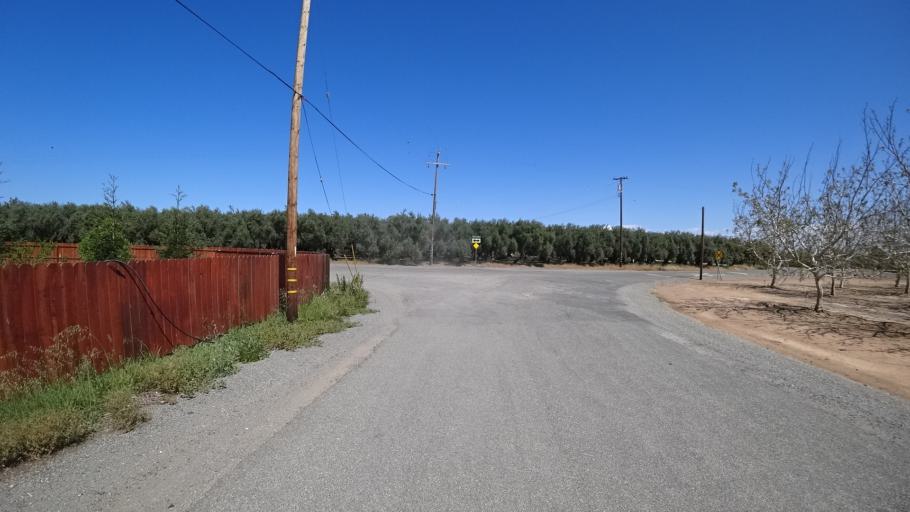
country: US
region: California
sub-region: Glenn County
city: Orland
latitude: 39.7976
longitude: -122.1795
